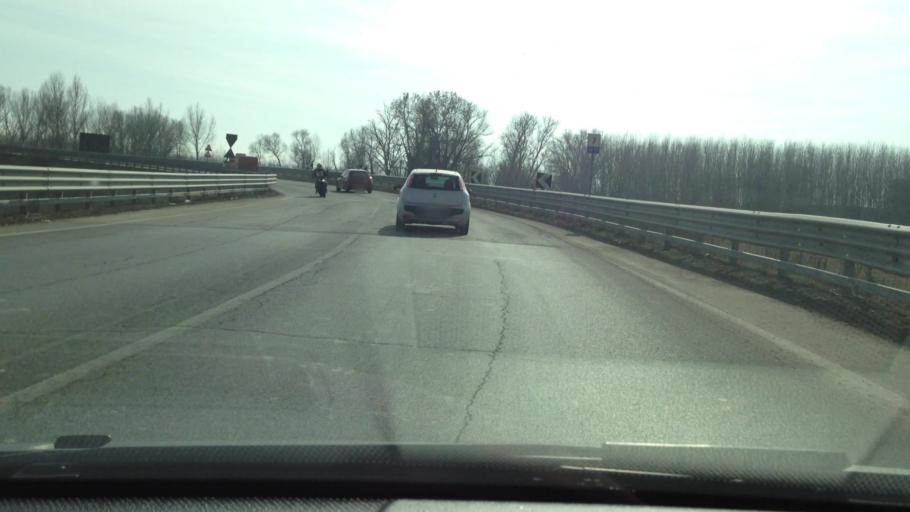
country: IT
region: Piedmont
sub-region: Provincia di Alessandria
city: Felizzano
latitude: 44.8926
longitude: 8.4384
